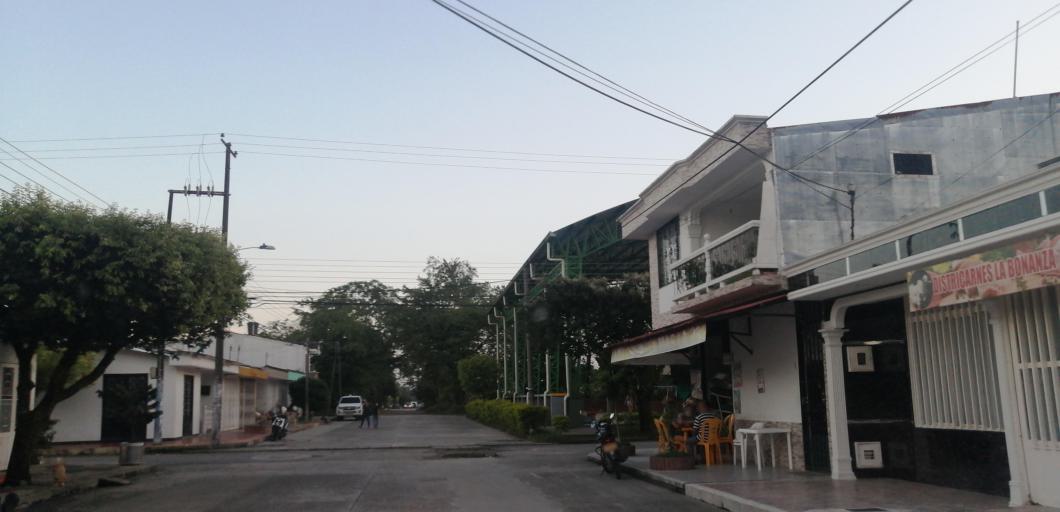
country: CO
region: Meta
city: Acacias
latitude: 3.9955
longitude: -73.7576
